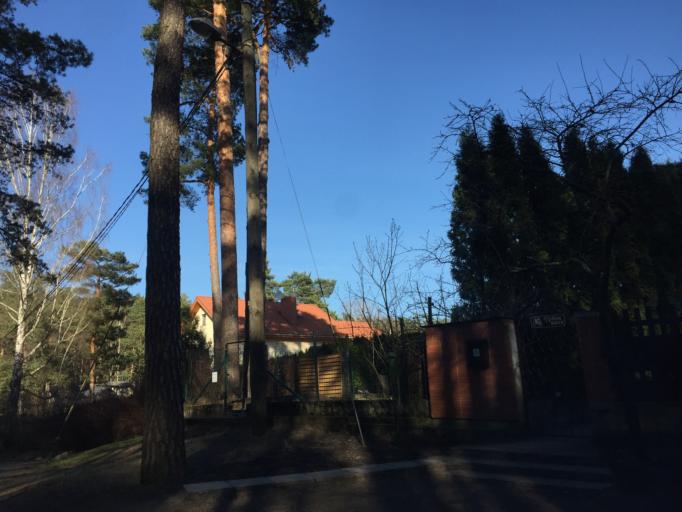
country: LV
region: Riga
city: Bergi
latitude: 56.9887
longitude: 24.2889
